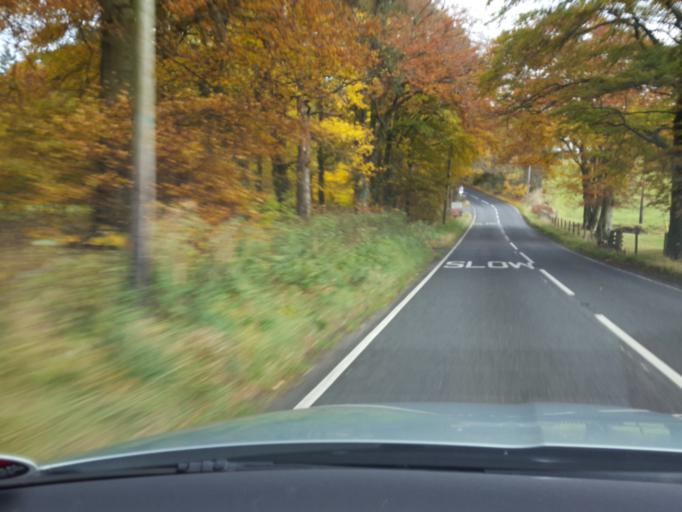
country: GB
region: Scotland
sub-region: The Scottish Borders
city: West Linton
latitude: 55.6848
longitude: -3.4155
